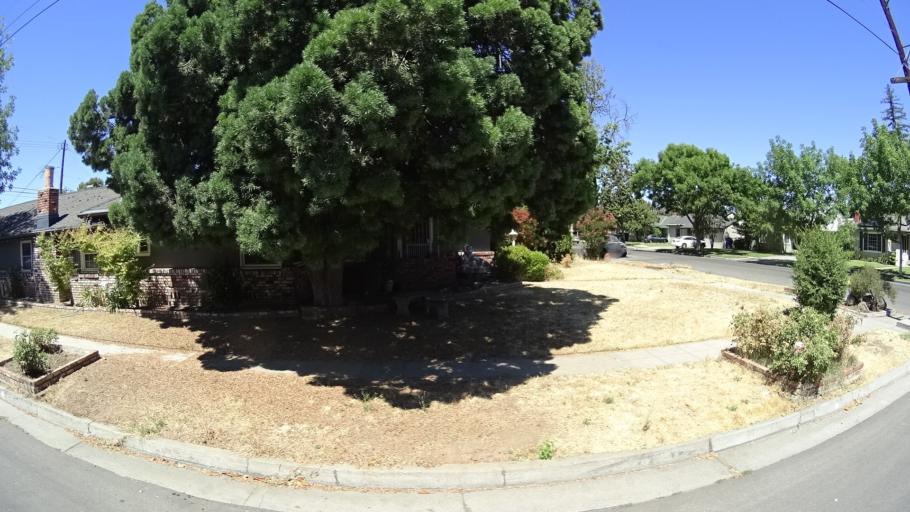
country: US
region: California
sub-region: Fresno County
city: Fresno
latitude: 36.7839
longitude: -119.8108
